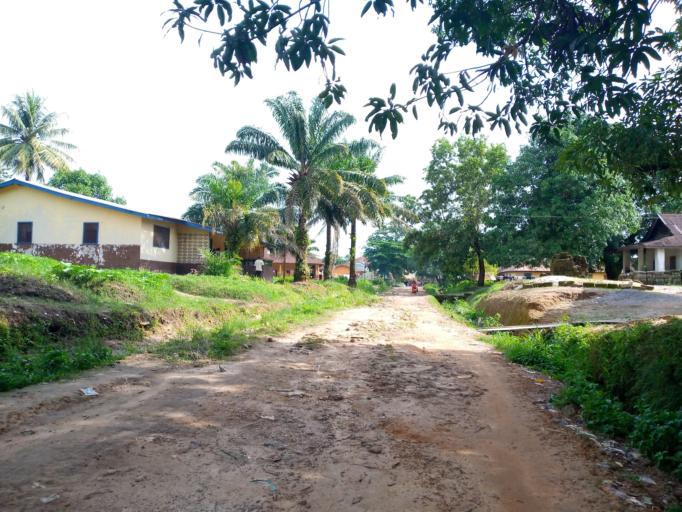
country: SL
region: Northern Province
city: Magburaka
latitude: 8.7243
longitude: -11.9468
